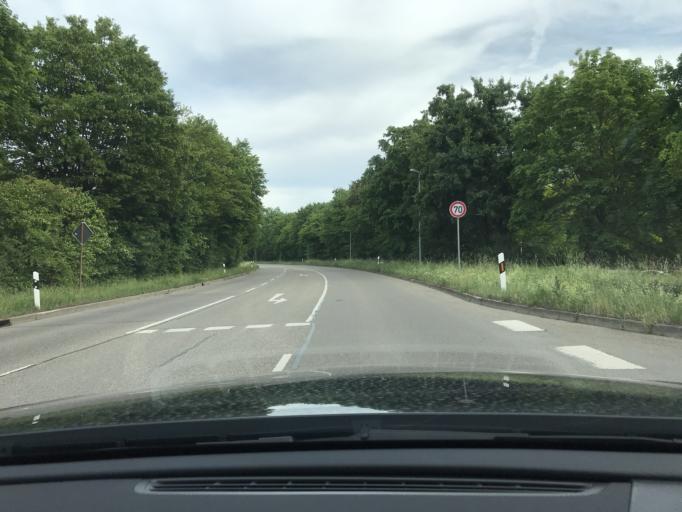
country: DE
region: Baden-Wuerttemberg
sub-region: Regierungsbezirk Stuttgart
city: Waiblingen
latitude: 48.8267
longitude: 9.3313
